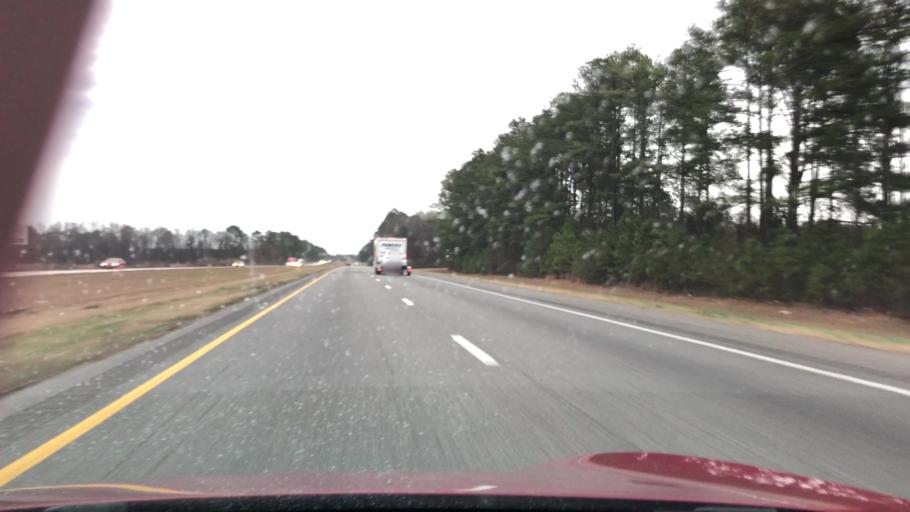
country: US
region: South Carolina
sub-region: Dillon County
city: Latta
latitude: 34.3863
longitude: -79.4670
